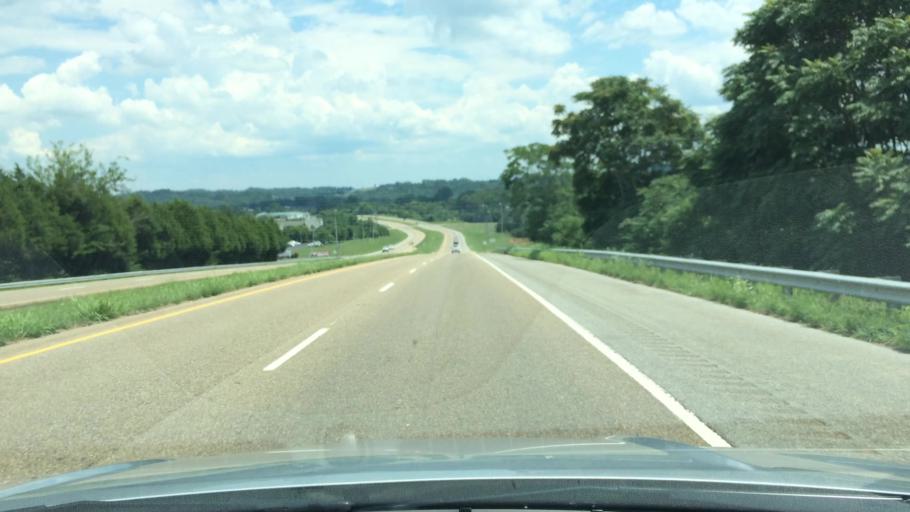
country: US
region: Tennessee
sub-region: Hamblen County
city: Morristown
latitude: 36.1695
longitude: -83.3836
